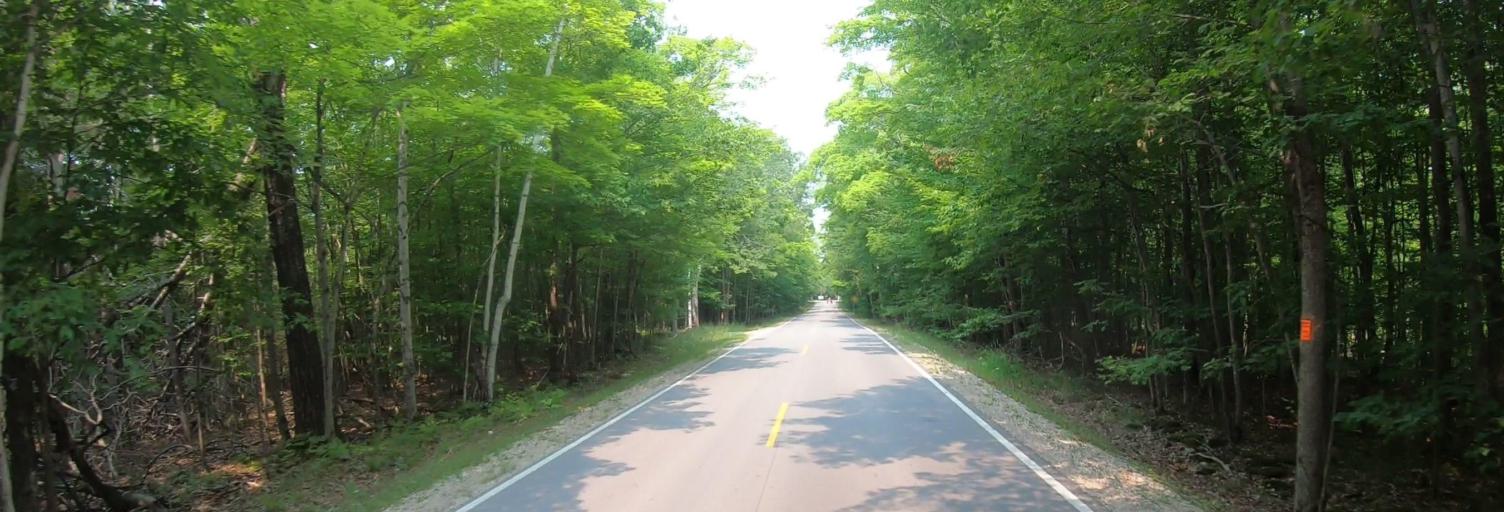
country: CA
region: Ontario
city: Thessalon
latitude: 46.0099
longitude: -83.6976
